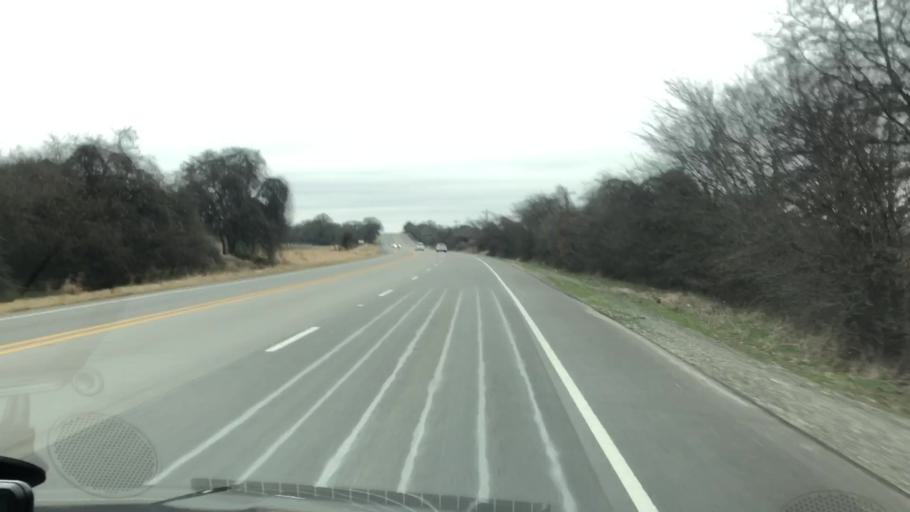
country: US
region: Texas
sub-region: Hamilton County
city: Hico
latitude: 32.0953
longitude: -98.1065
